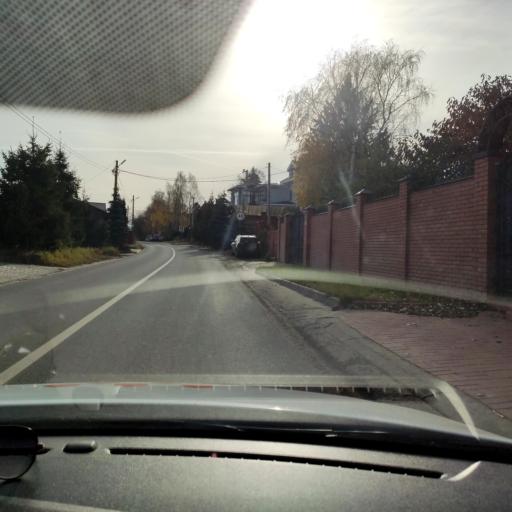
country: RU
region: Tatarstan
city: Verkhniy Uslon
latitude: 55.6230
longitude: 49.0138
